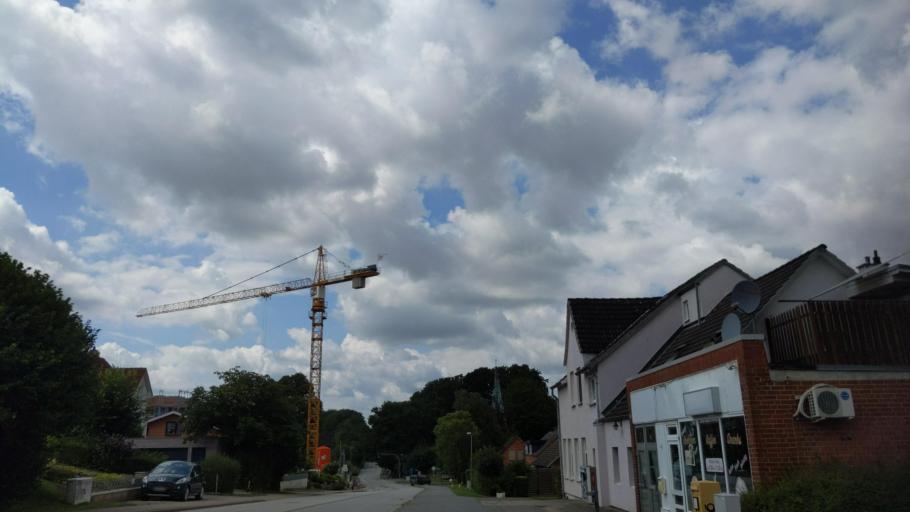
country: DE
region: Schleswig-Holstein
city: Hamberge
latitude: 53.8385
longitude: 10.5820
